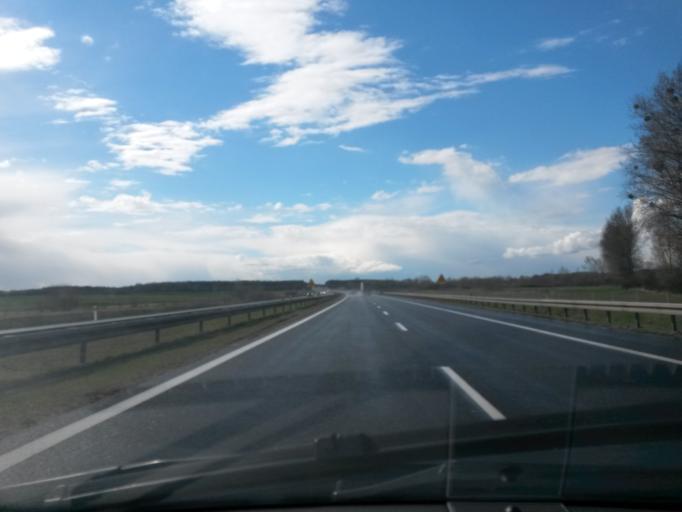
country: PL
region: Greater Poland Voivodeship
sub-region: Powiat slupecki
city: Strzalkowo
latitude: 52.2615
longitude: 17.7797
